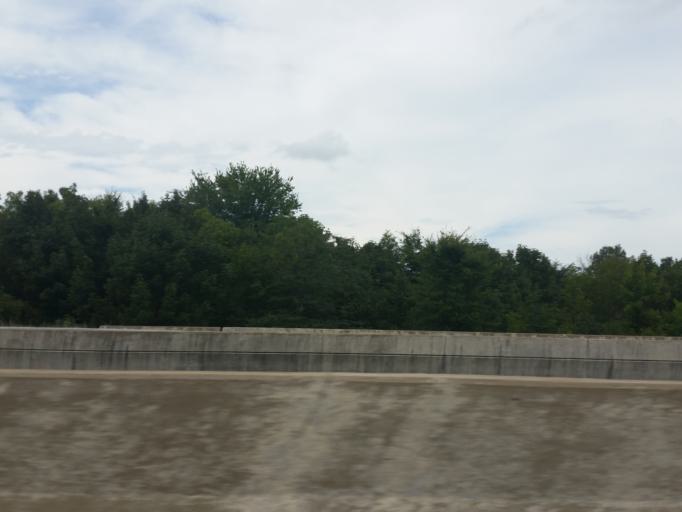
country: US
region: Kentucky
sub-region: Lyon County
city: Eddyville
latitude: 37.0700
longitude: -88.1477
